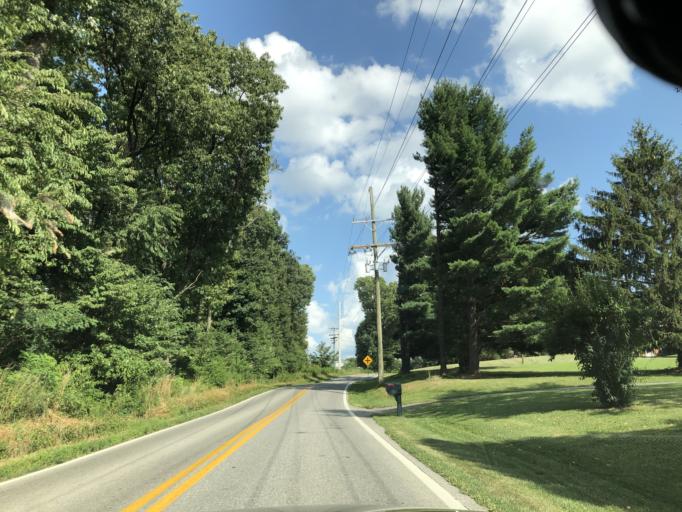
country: US
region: Maryland
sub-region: Carroll County
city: Mount Airy
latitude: 39.3960
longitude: -77.1847
